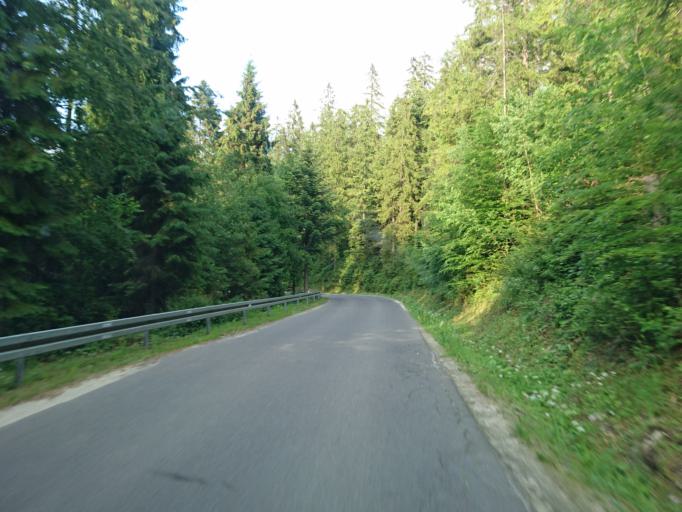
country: PL
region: Lesser Poland Voivodeship
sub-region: Powiat nowotarski
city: Lopuszna
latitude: 49.4993
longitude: 20.1801
